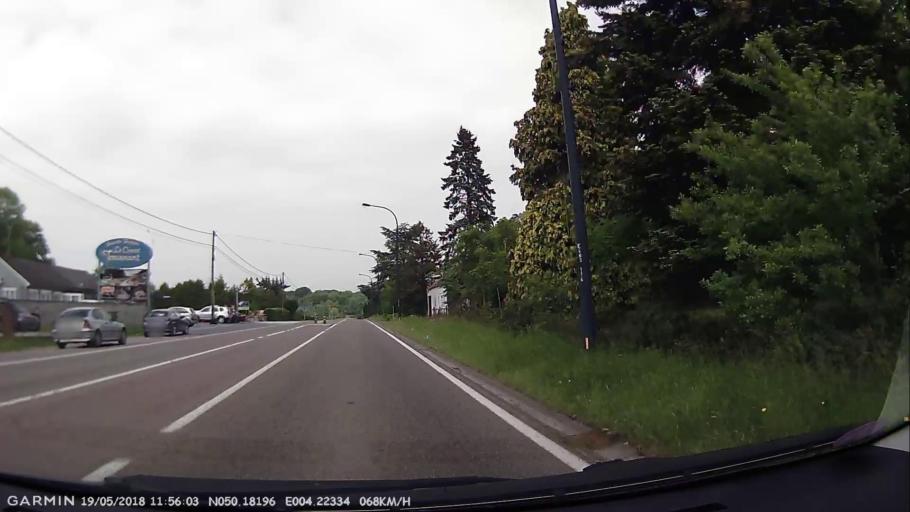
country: BE
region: Wallonia
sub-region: Province du Hainaut
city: Beaumont
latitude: 50.1822
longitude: 4.2231
